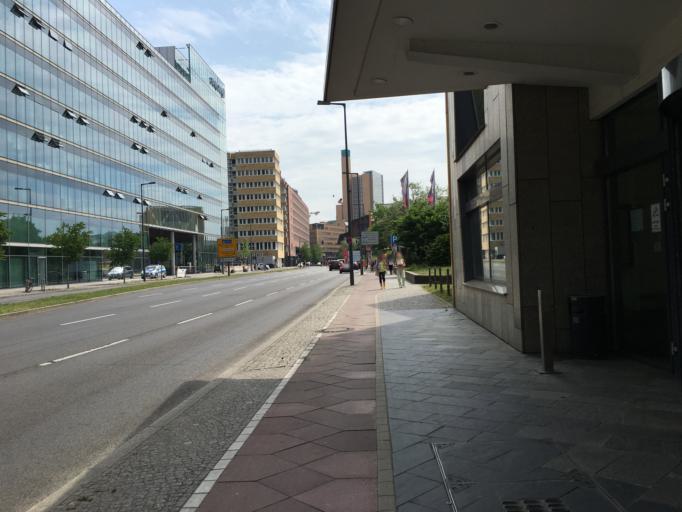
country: DE
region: Berlin
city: Tiergarten Bezirk
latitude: 52.5104
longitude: 13.3712
